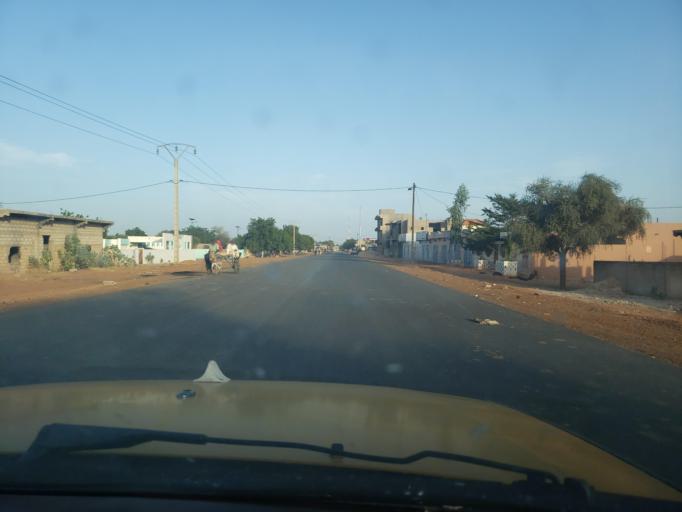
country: SN
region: Louga
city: Dara
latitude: 15.3497
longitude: -15.4919
